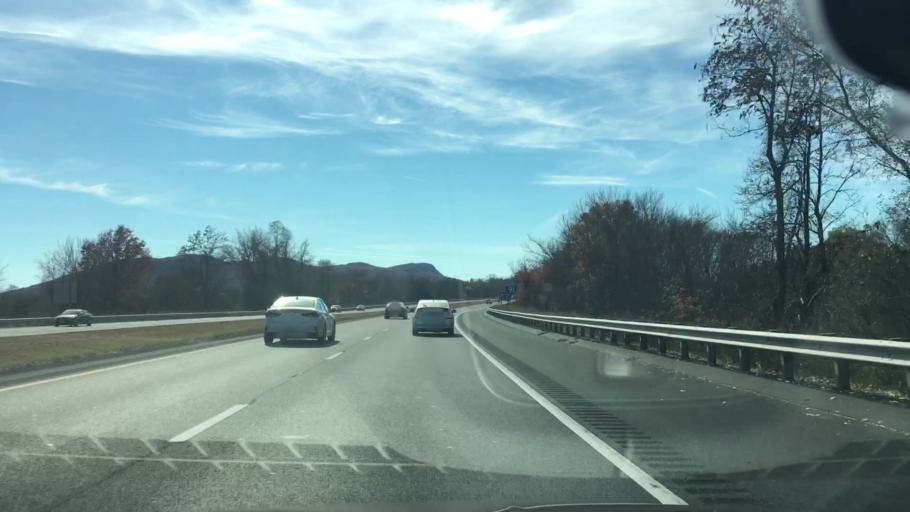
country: US
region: Massachusetts
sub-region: Hampshire County
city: Northampton
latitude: 42.3165
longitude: -72.6166
